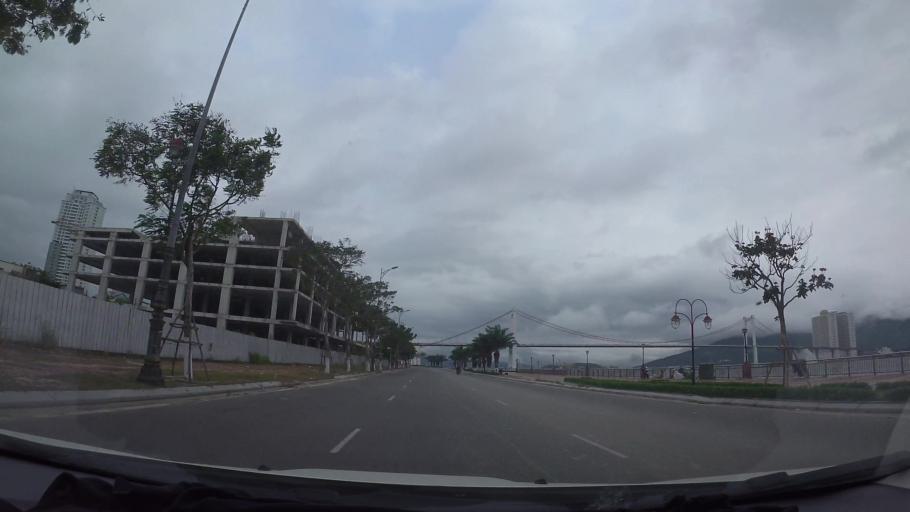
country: VN
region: Da Nang
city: Da Nang
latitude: 16.0895
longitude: 108.2201
